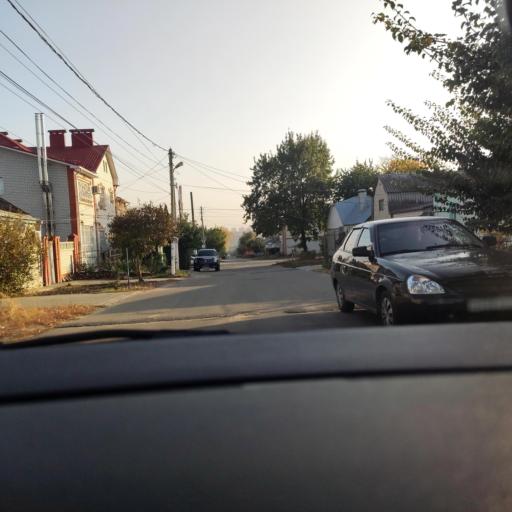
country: RU
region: Voronezj
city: Podgornoye
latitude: 51.6974
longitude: 39.1532
